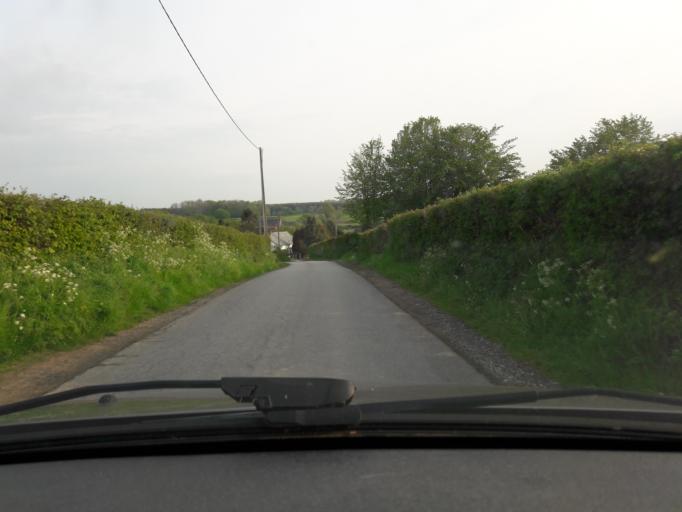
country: FR
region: Nord-Pas-de-Calais
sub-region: Departement du Nord
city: Marpent
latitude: 50.2419
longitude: 4.0779
